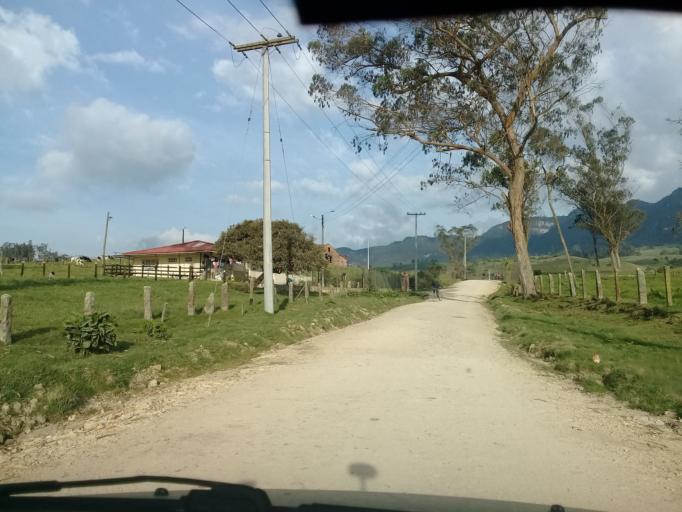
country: CO
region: Cundinamarca
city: Sibate
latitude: 4.4272
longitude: -74.2895
